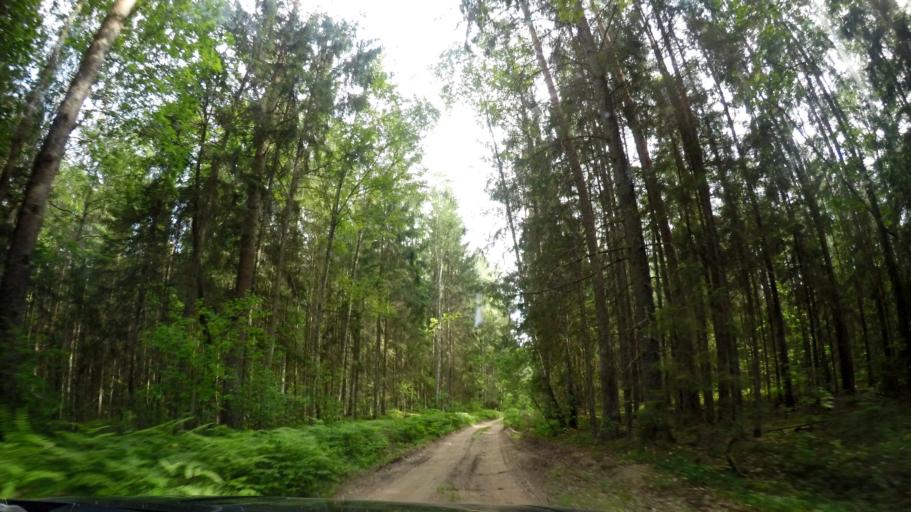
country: BY
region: Grodnenskaya
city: Skidal'
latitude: 53.8292
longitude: 24.1787
